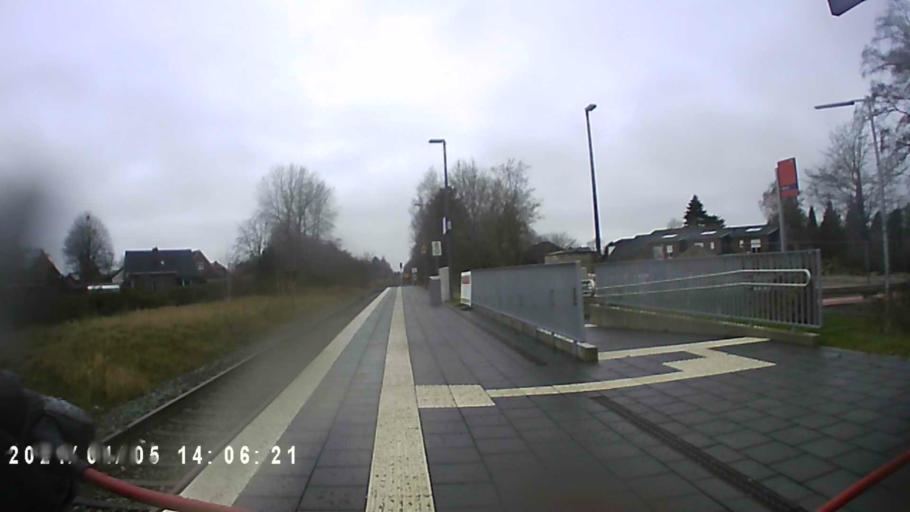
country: DE
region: Lower Saxony
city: Weener
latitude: 53.1635
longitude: 7.3428
